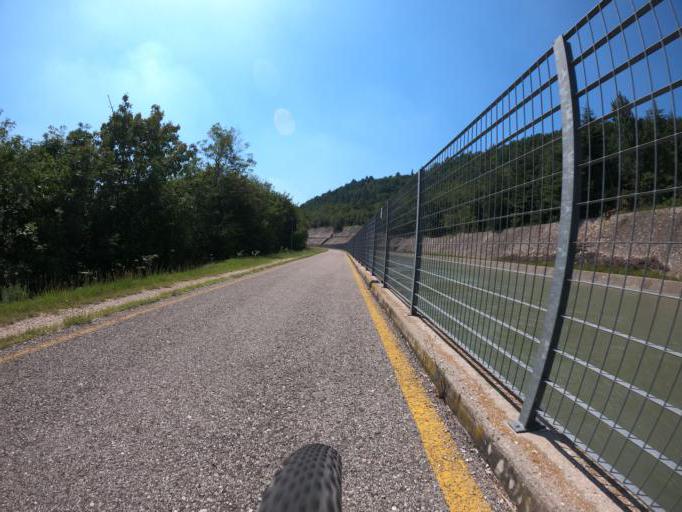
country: IT
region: Veneto
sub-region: Provincia di Verona
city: Volargne
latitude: 45.5523
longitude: 10.8209
